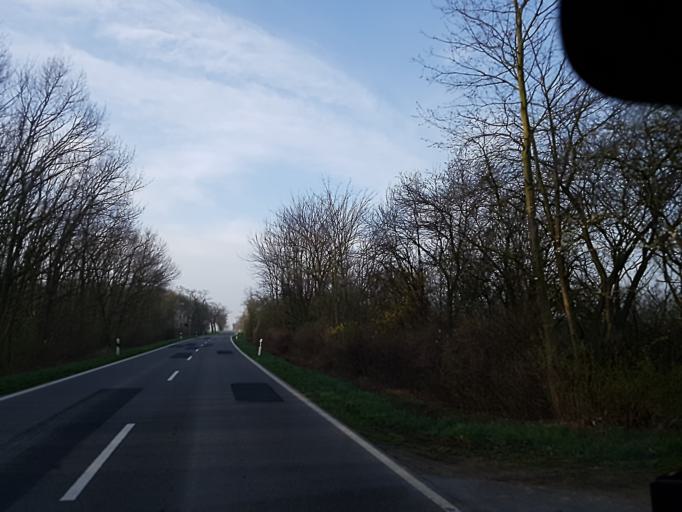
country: DE
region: Brandenburg
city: Muhlberg
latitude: 51.4435
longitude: 13.2690
